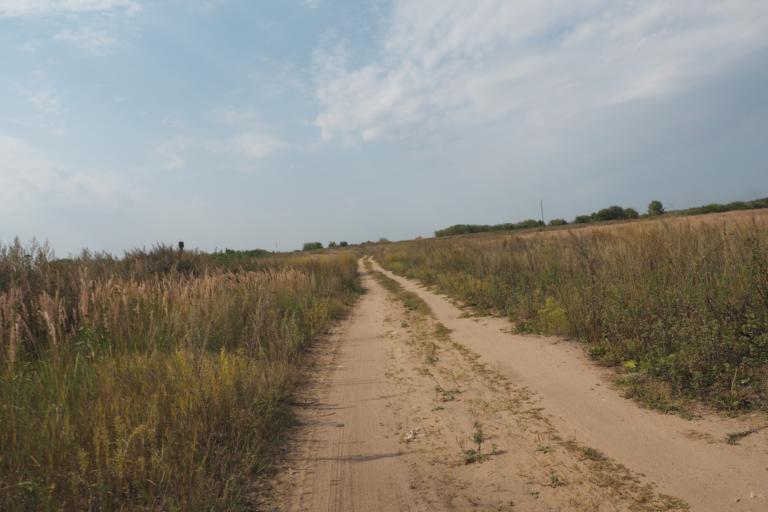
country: RU
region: Moskovskaya
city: Ramenskoye
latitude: 55.5571
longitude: 38.2911
